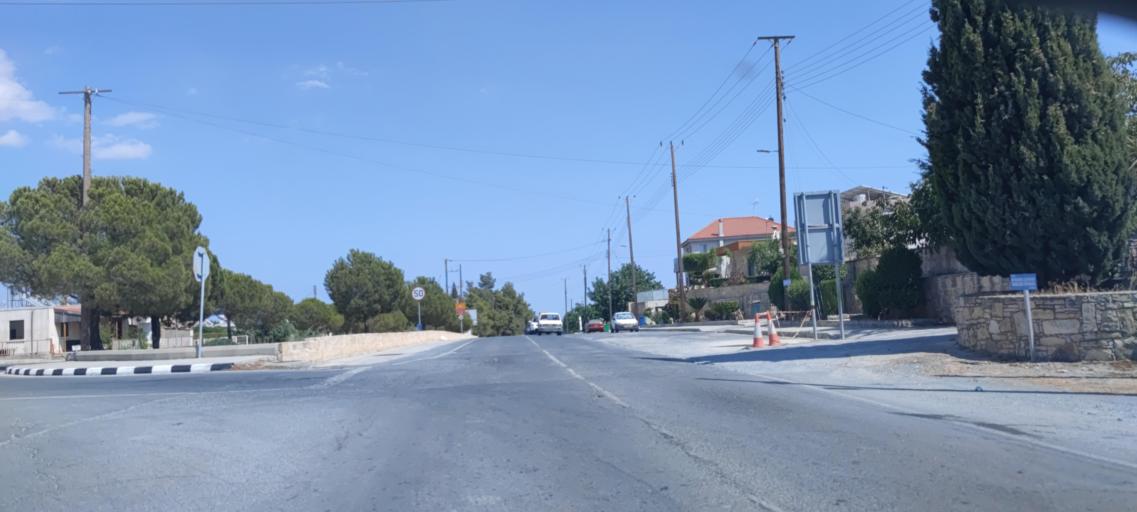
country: CY
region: Limassol
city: Sotira
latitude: 34.7589
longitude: 32.8517
